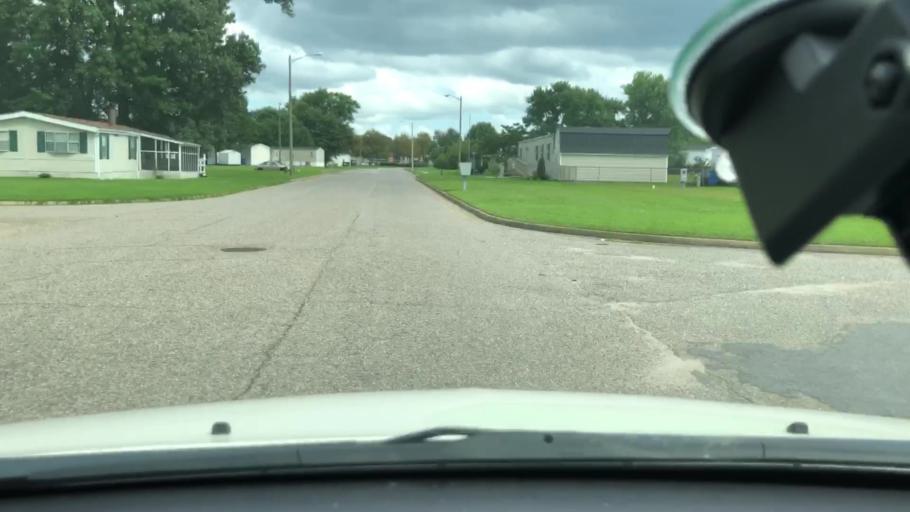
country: US
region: Virginia
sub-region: City of Chesapeake
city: Chesapeake
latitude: 36.7786
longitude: -76.2729
